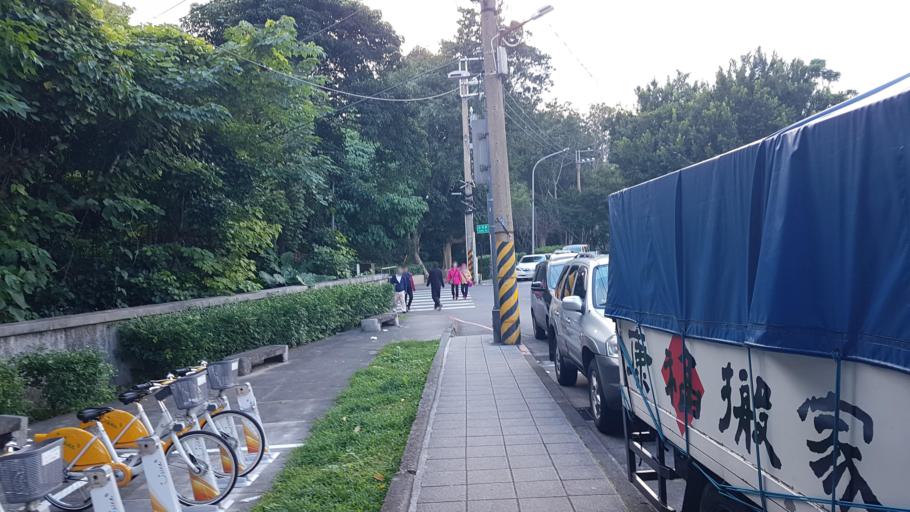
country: TW
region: Taipei
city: Taipei
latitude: 25.1406
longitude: 121.5047
